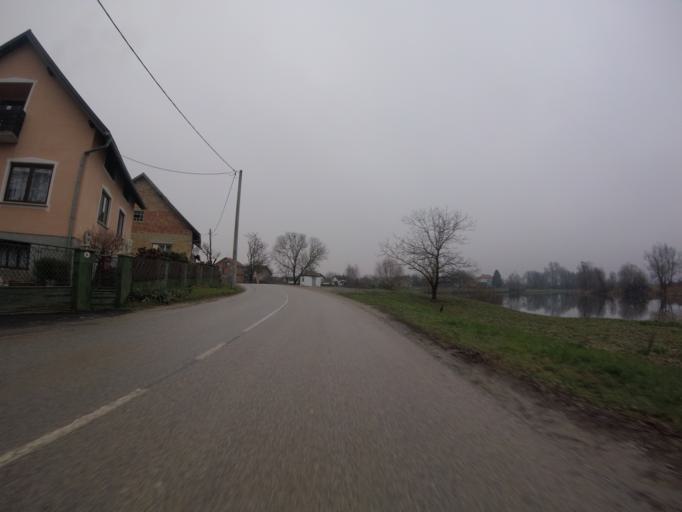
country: HR
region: Sisacko-Moslavacka
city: Lekenik
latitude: 45.6544
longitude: 16.2614
